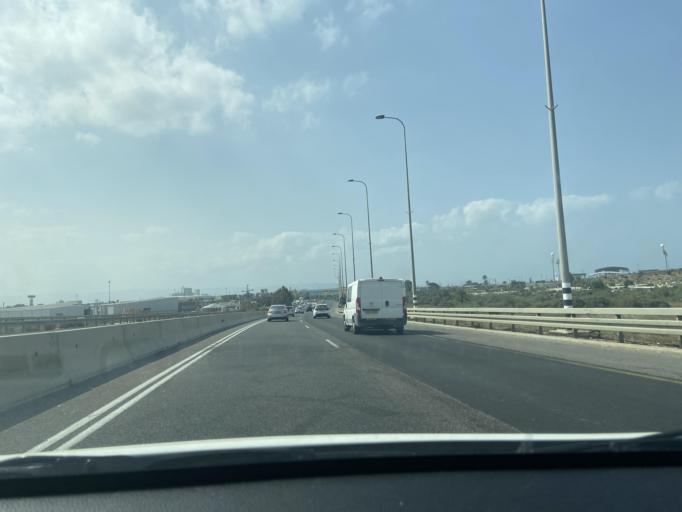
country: IL
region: Northern District
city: `Akko
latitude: 32.9102
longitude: 35.0943
